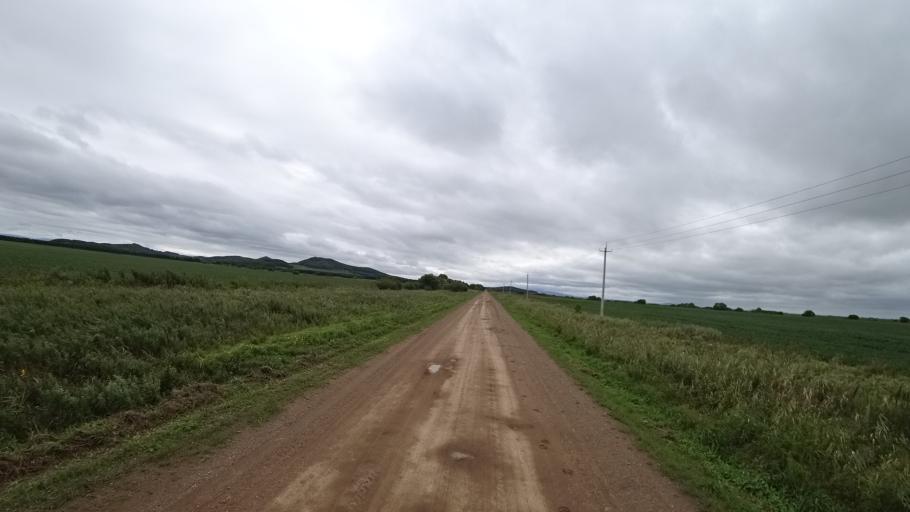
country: RU
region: Primorskiy
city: Chernigovka
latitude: 44.4926
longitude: 132.5716
